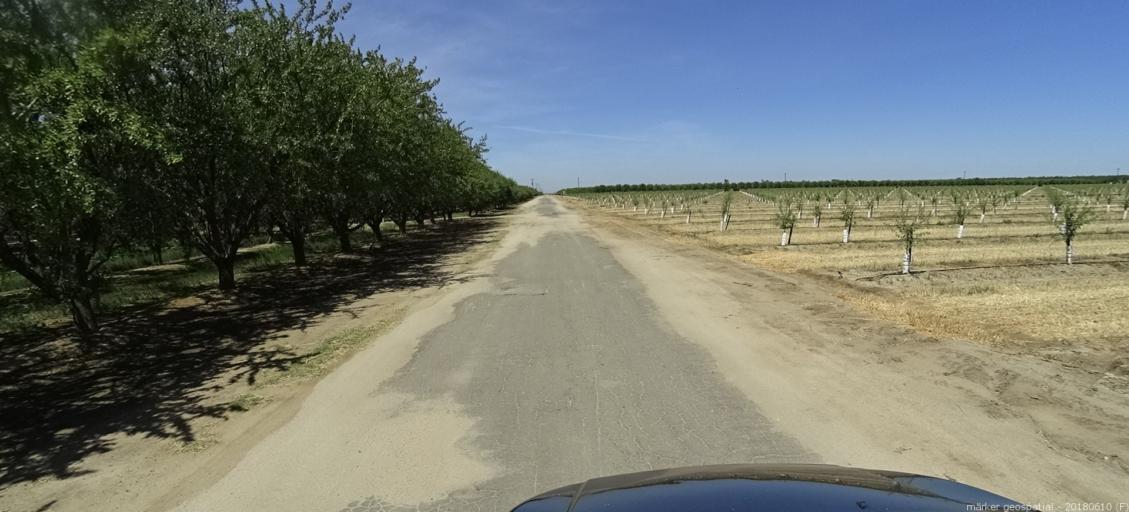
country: US
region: California
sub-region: Madera County
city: Chowchilla
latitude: 37.0399
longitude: -120.4067
